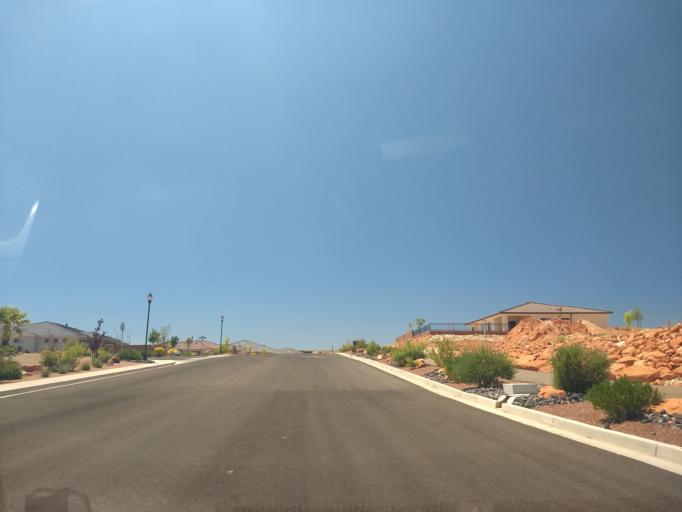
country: US
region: Utah
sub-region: Washington County
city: Washington
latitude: 37.1590
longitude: -113.5293
